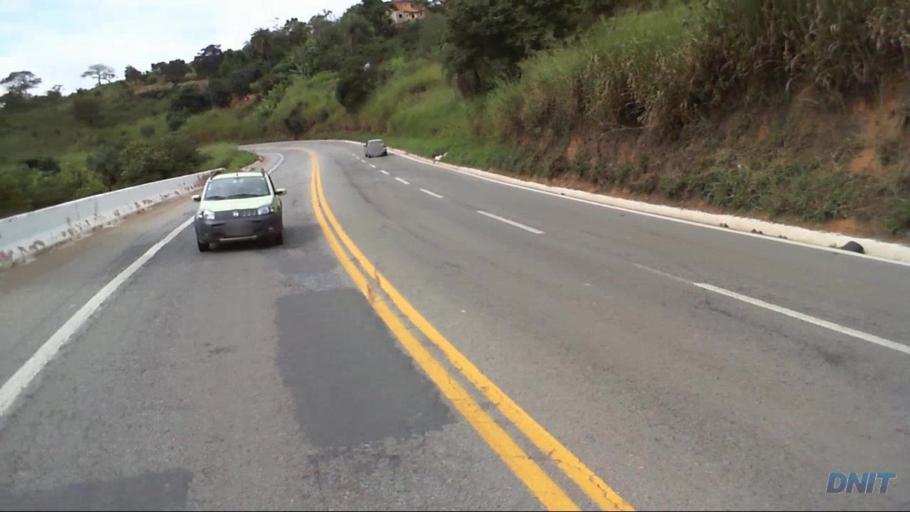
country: BR
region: Minas Gerais
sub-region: Caete
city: Caete
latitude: -19.7600
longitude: -43.6385
